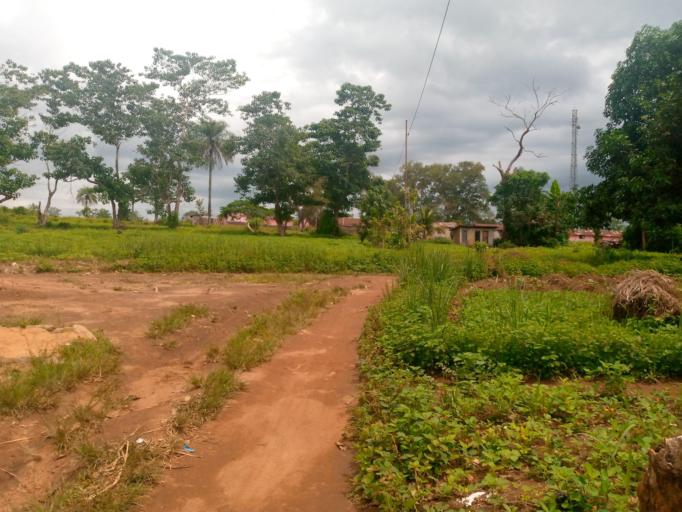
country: SL
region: Southern Province
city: Mogbwemo
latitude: 7.6007
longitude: -12.1717
